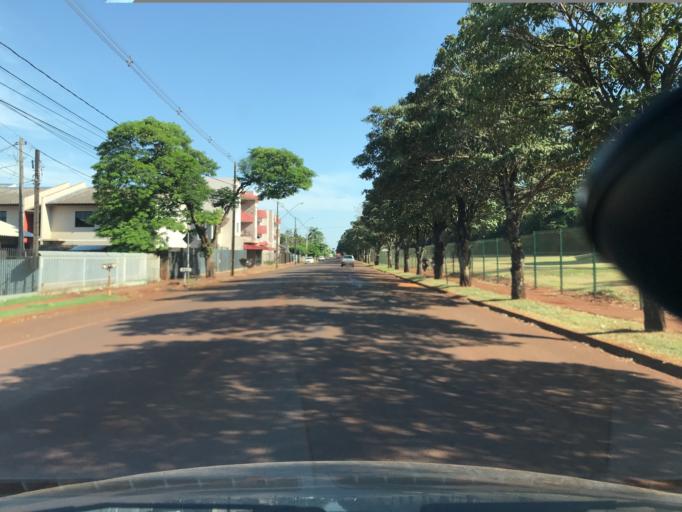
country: BR
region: Parana
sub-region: Palotina
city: Palotina
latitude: -24.2949
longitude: -53.8437
